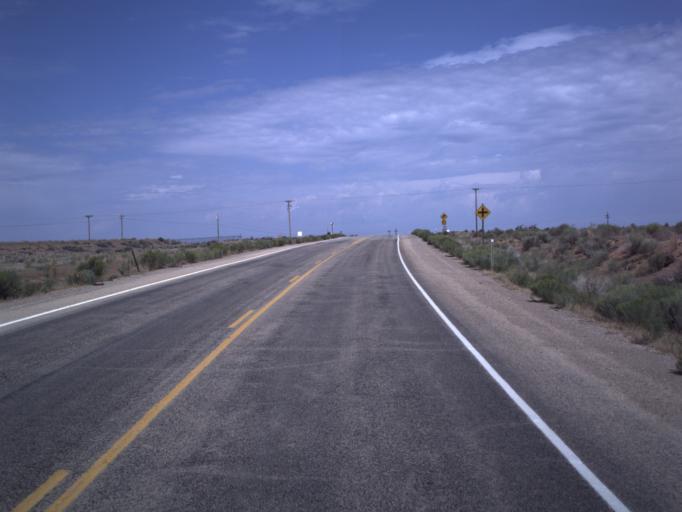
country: US
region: Utah
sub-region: Uintah County
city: Naples
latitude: 40.1833
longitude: -109.3278
